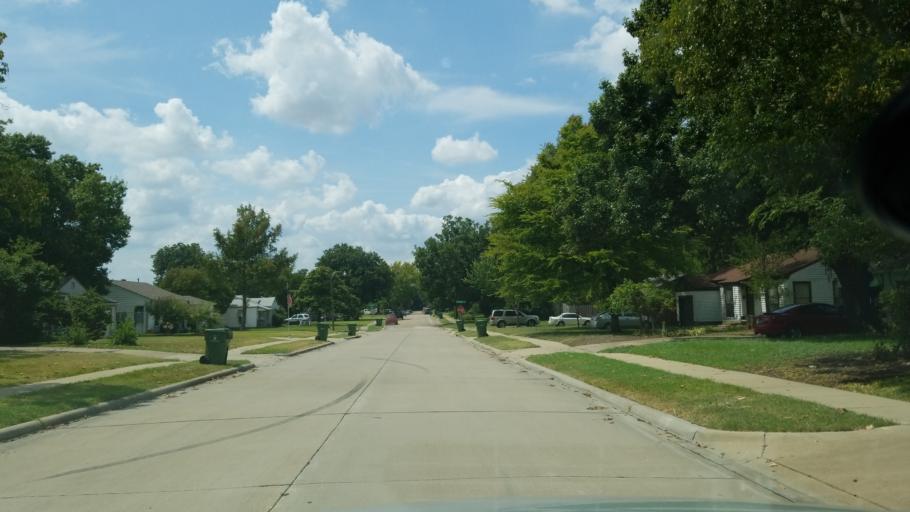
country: US
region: Texas
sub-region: Dallas County
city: Garland
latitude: 32.9181
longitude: -96.6511
